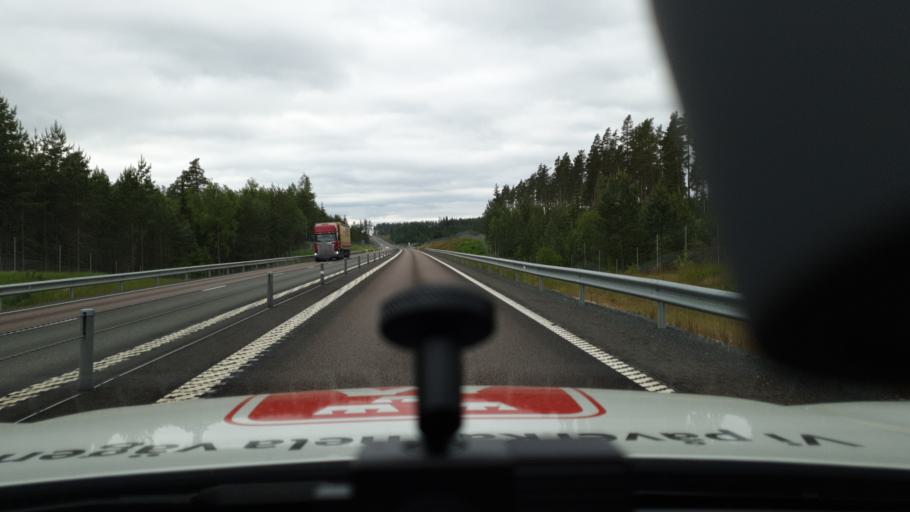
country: SE
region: Joenkoeping
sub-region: Mullsjo Kommun
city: Mullsjoe
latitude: 57.8687
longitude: 13.9599
